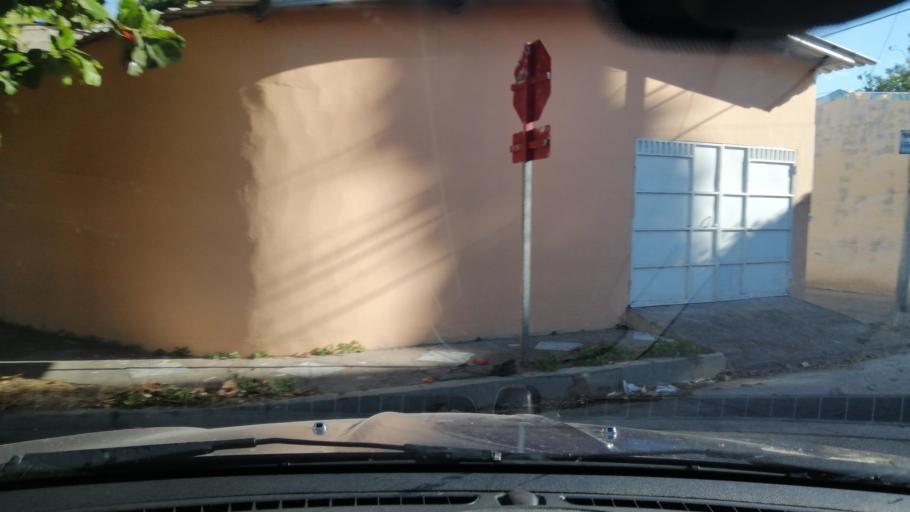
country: SV
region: Santa Ana
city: Metapan
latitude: 14.3338
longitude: -89.4497
